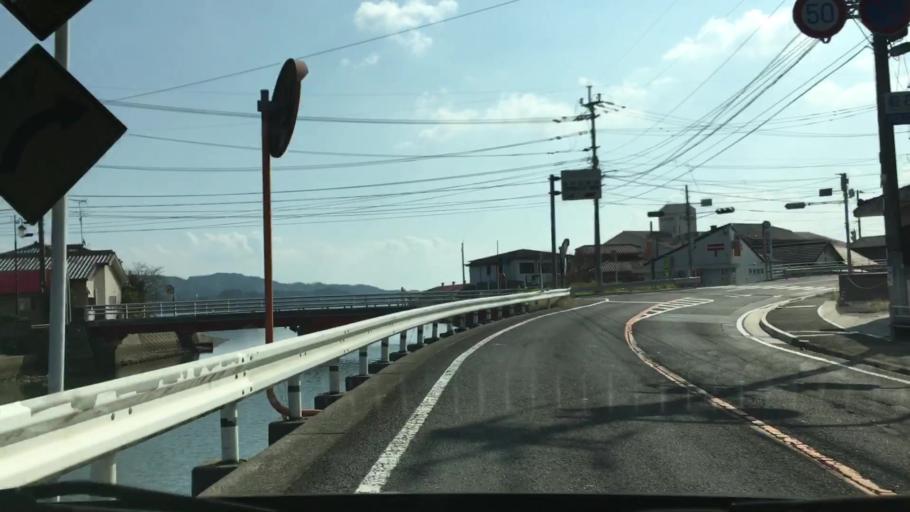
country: JP
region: Nagasaki
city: Togitsu
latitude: 32.9505
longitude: 129.7852
